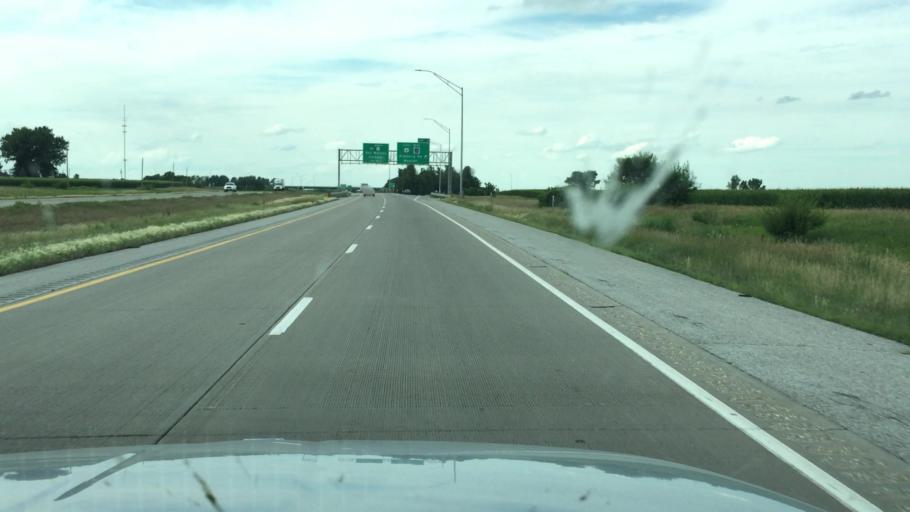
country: US
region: Iowa
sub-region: Scott County
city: Walcott
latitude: 41.5845
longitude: -90.6759
